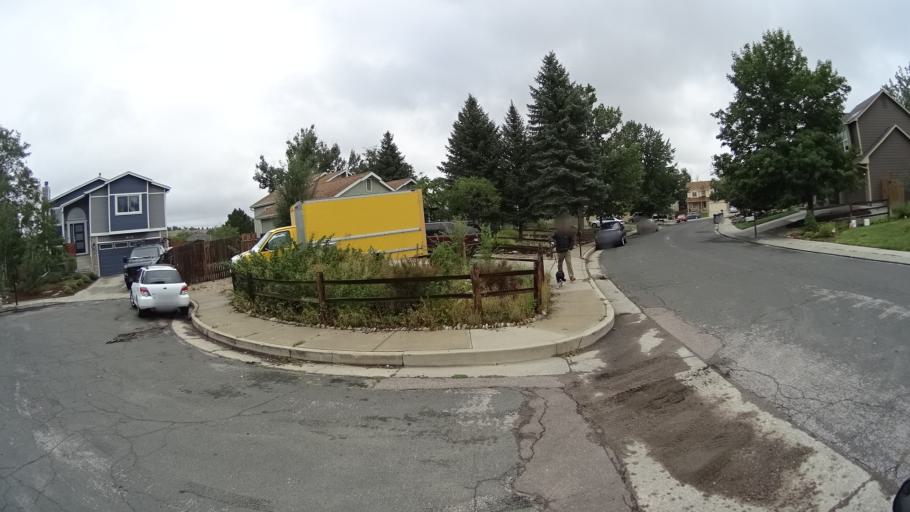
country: US
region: Colorado
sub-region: El Paso County
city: Cimarron Hills
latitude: 38.9285
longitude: -104.7647
